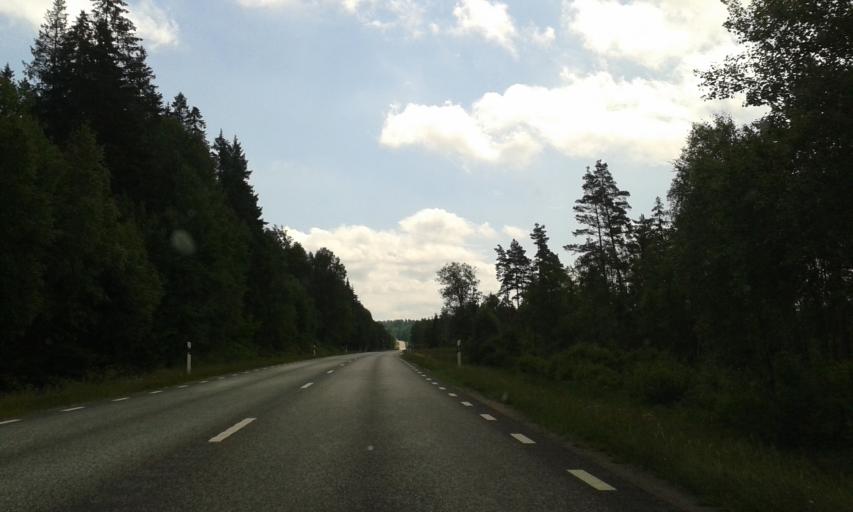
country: SE
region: Joenkoeping
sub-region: Gislaveds Kommun
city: Reftele
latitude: 57.2372
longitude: 13.6614
